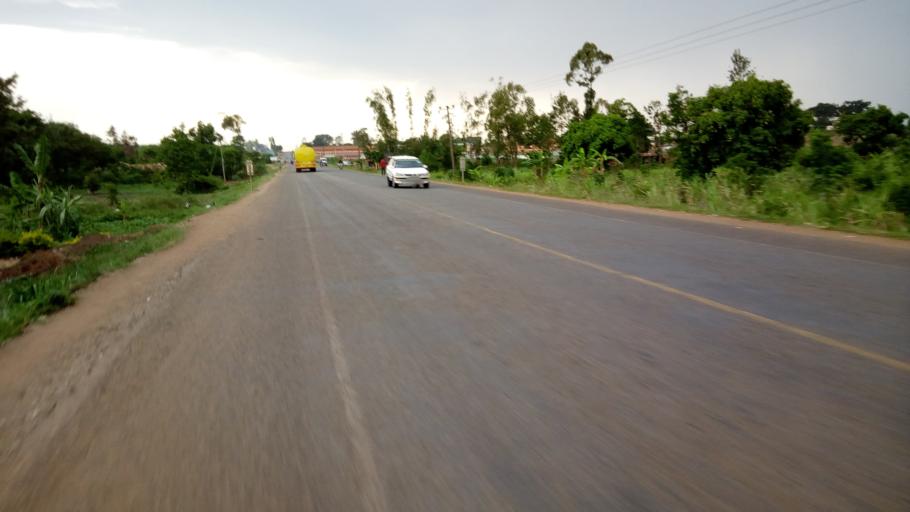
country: UG
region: Eastern Region
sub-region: Mbale District
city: Mbale
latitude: 1.1086
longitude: 34.1726
